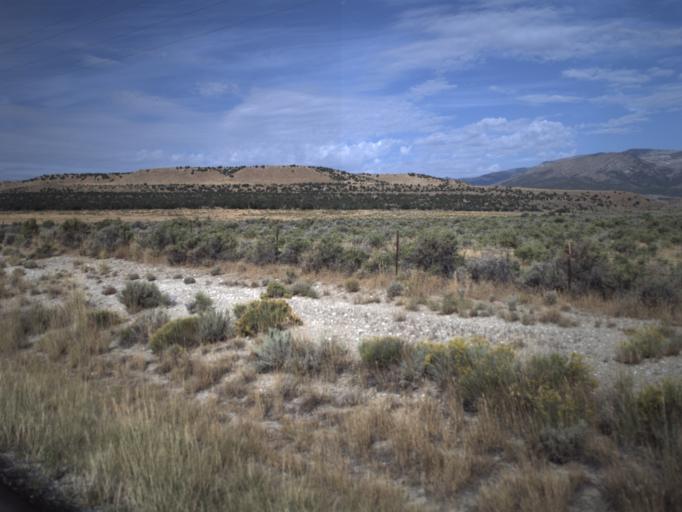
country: US
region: Idaho
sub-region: Minidoka County
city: Heyburn
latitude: 41.8221
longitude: -113.1890
